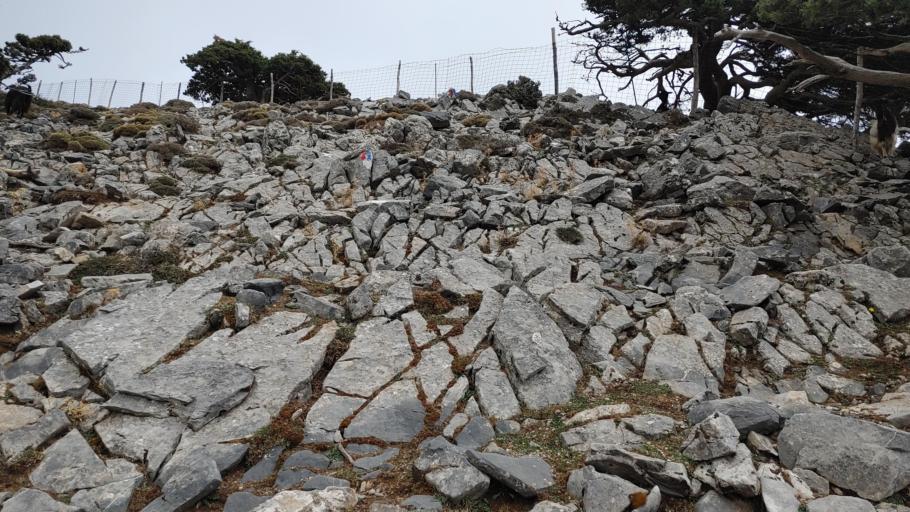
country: GR
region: Crete
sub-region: Nomos Chanias
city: Perivolia
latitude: 35.3164
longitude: 23.9277
